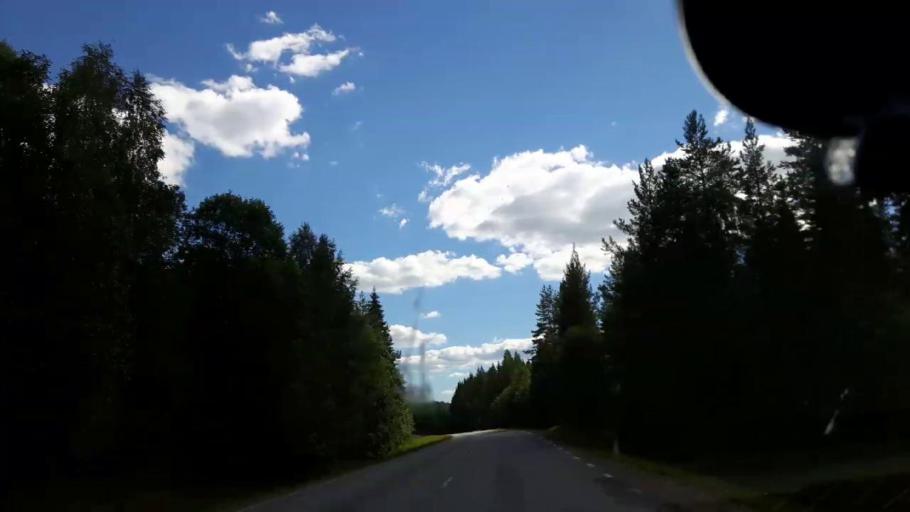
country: SE
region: Jaemtland
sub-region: Ragunda Kommun
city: Hammarstrand
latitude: 62.9536
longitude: 16.2096
